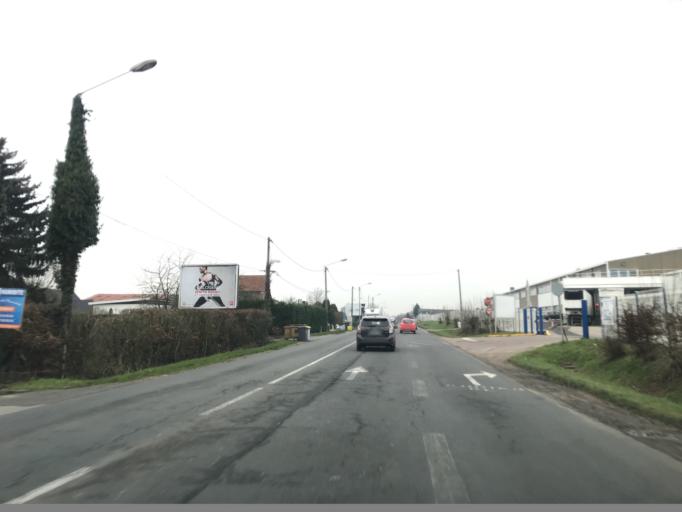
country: FR
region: Haute-Normandie
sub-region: Departement de la Seine-Maritime
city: Boos
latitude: 49.3961
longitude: 1.1826
